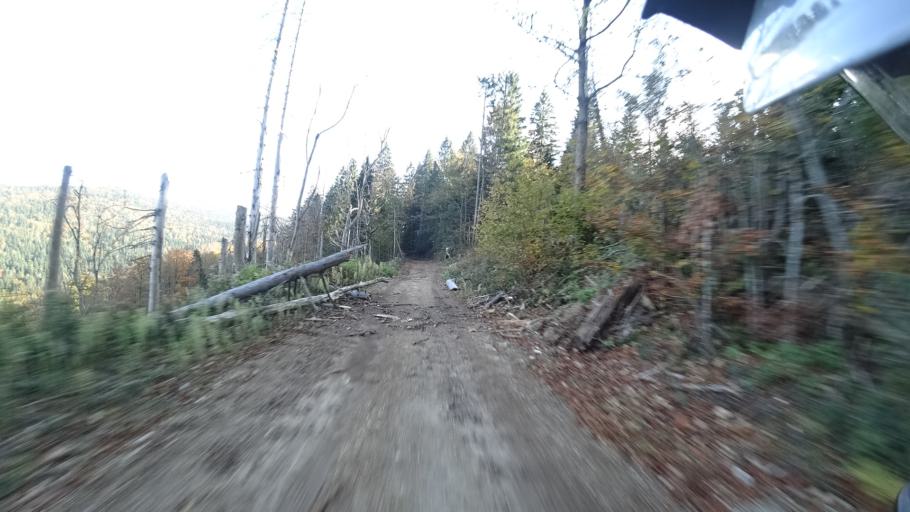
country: HR
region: Karlovacka
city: Plaski
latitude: 44.9546
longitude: 15.4479
